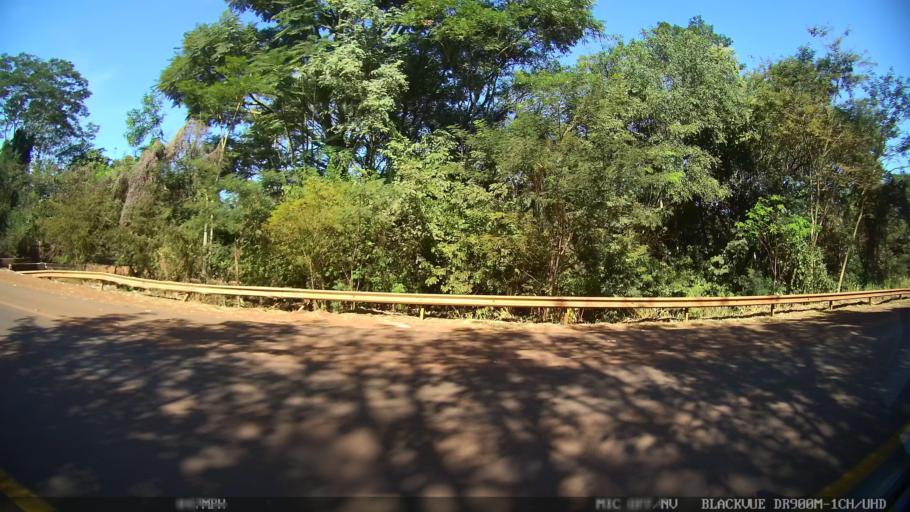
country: BR
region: Sao Paulo
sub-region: Barretos
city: Barretos
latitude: -20.4508
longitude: -48.4546
